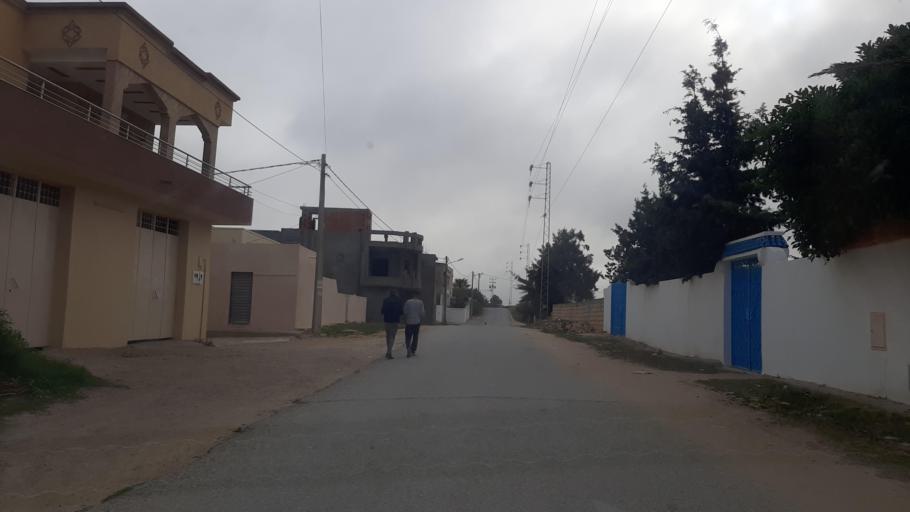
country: TN
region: Nabul
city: Menzel Heurr
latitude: 36.6786
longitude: 10.9241
